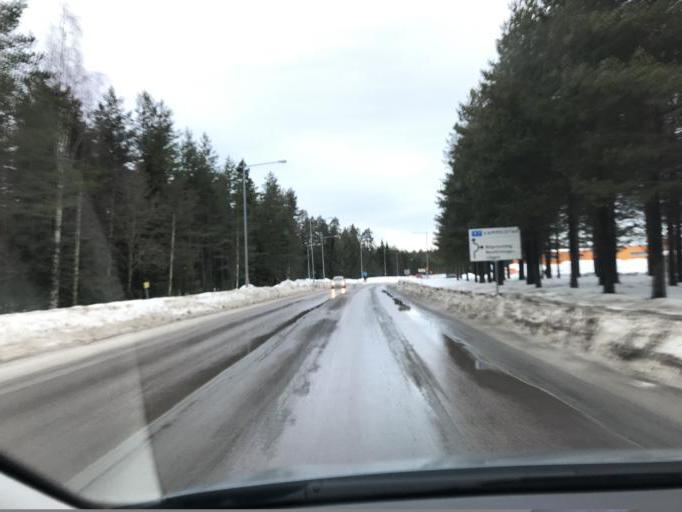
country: SE
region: Norrbotten
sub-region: Lulea Kommun
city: Gammelstad
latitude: 65.6177
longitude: 22.0388
